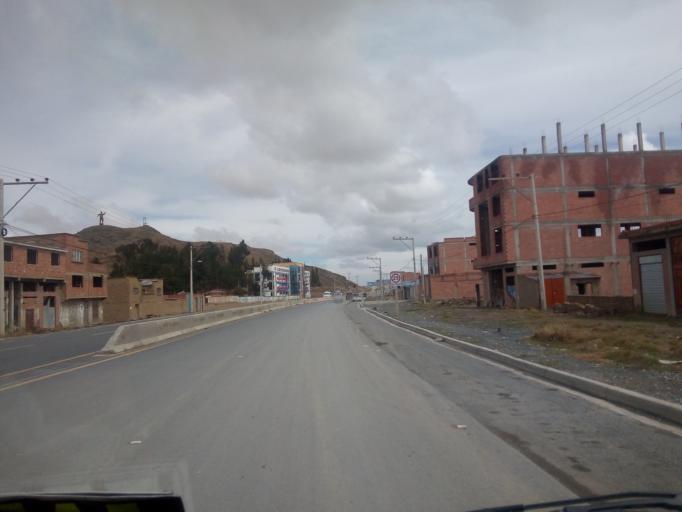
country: BO
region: La Paz
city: Achacachi
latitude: -16.0540
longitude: -68.6807
